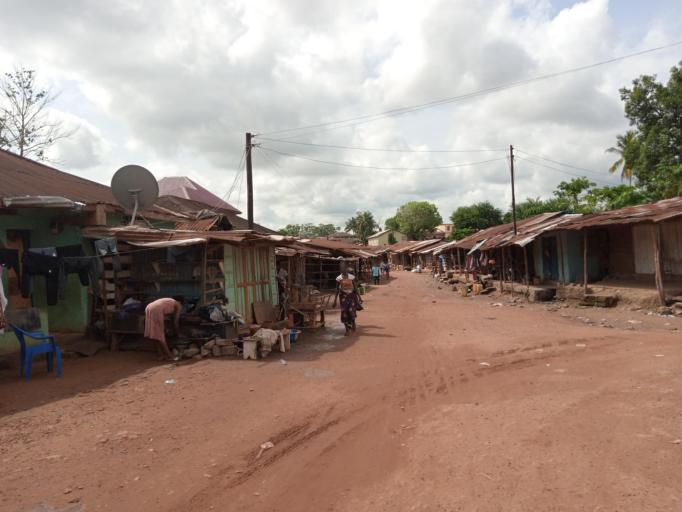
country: SL
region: Southern Province
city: Bo
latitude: 7.9642
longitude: -11.7373
